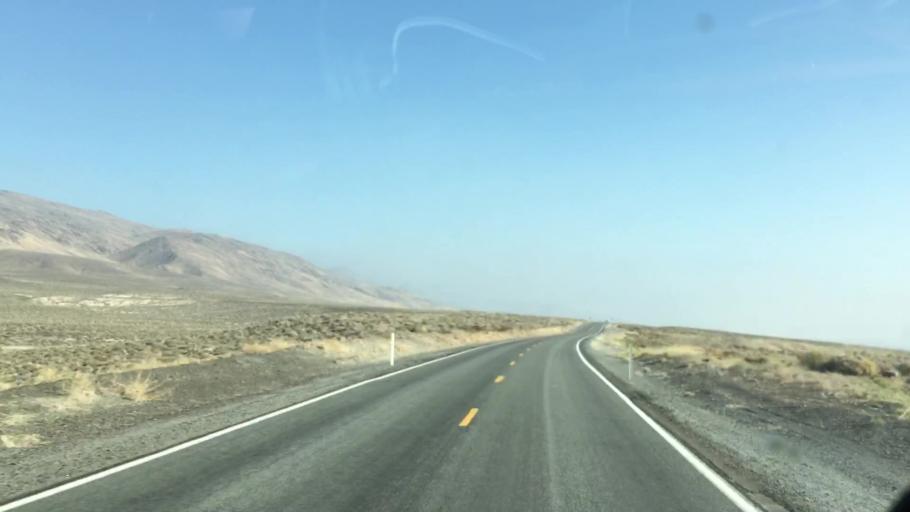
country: US
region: Nevada
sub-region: Lyon County
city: Fernley
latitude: 39.9304
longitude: -119.3834
